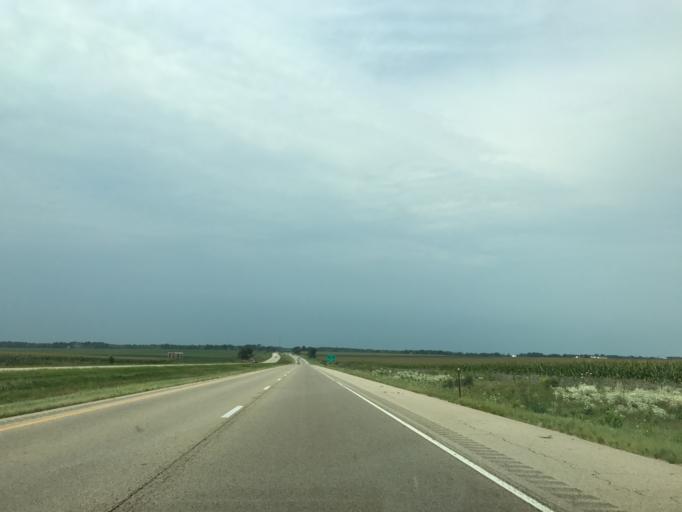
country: US
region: Illinois
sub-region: Bureau County
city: Depue
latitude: 41.4003
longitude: -89.3318
